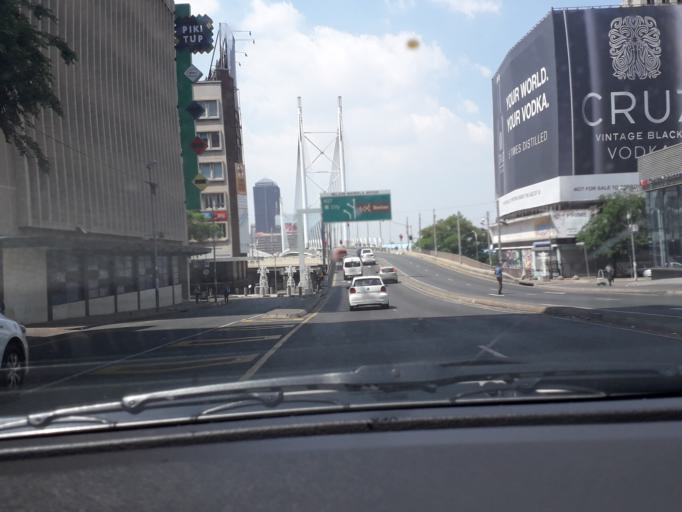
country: ZA
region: Gauteng
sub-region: City of Johannesburg Metropolitan Municipality
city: Johannesburg
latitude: -26.1941
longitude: 28.0336
